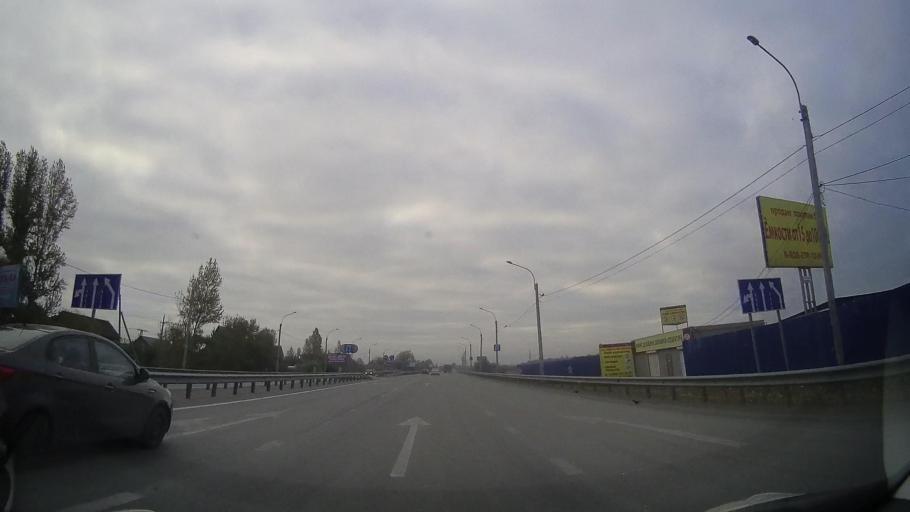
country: RU
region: Rostov
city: Bataysk
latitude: 47.1529
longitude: 39.7712
